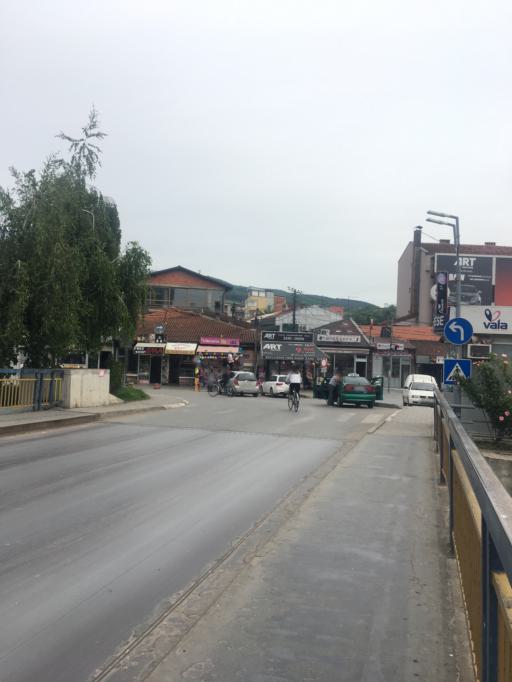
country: XK
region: Pec
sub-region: Komuna e Pejes
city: Peje
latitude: 42.6586
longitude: 20.2860
